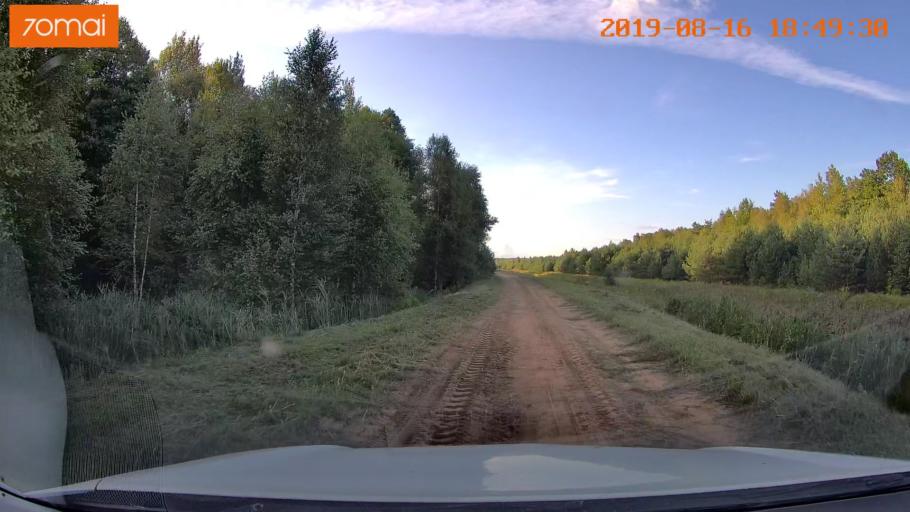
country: BY
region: Mogilev
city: Asipovichy
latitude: 53.2371
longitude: 28.6654
